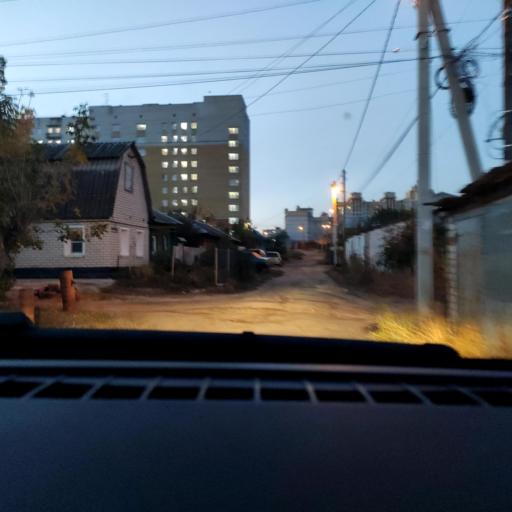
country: RU
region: Voronezj
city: Voronezh
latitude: 51.6787
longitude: 39.2465
